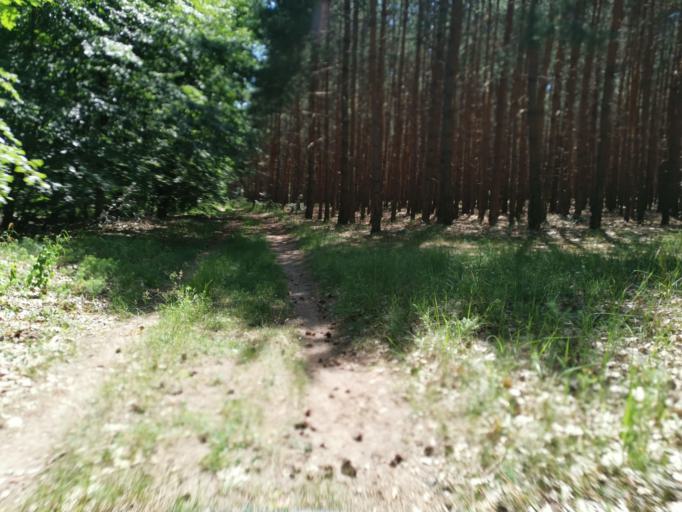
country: CZ
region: South Moravian
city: Rohatec
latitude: 48.9042
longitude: 17.2184
